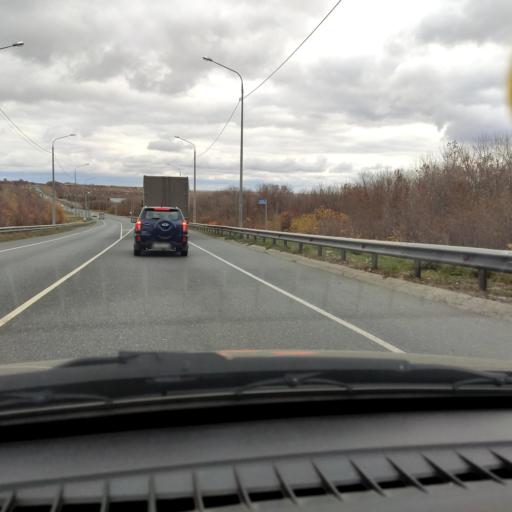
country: RU
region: Samara
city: Mezhdurechensk
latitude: 53.2477
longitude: 49.0150
